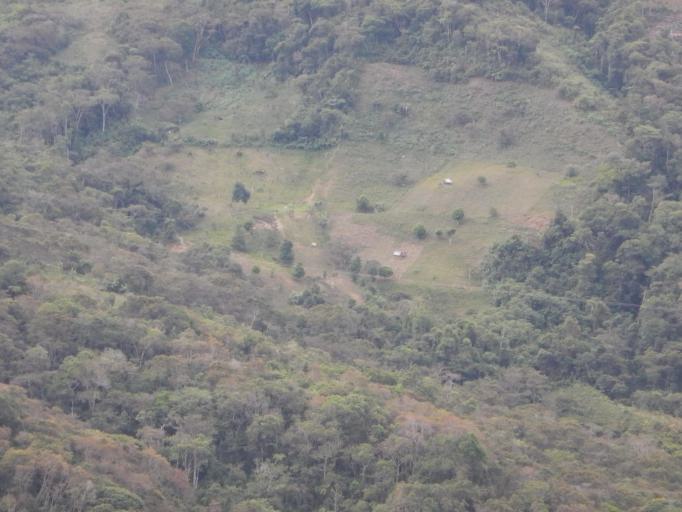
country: BO
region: La Paz
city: Coroico
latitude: -16.1287
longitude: -67.7575
